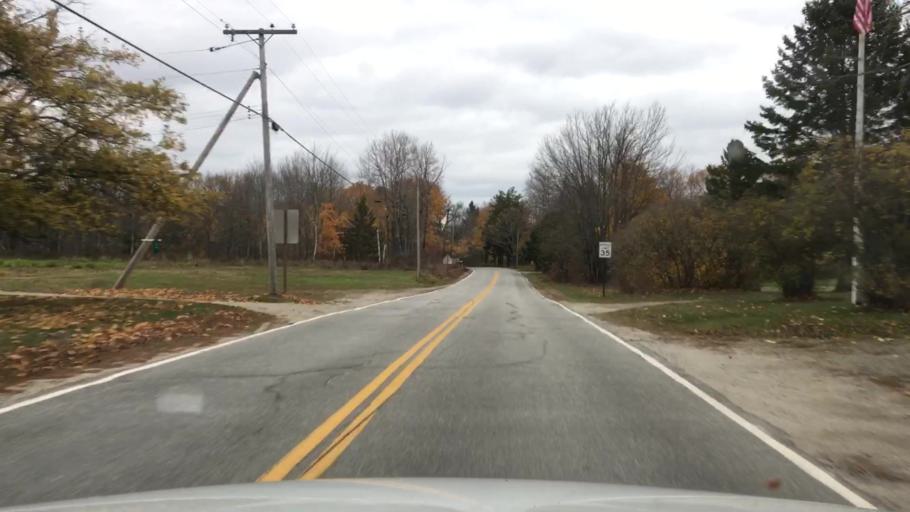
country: US
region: Maine
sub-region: Hancock County
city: Sedgwick
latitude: 44.2690
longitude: -68.5667
